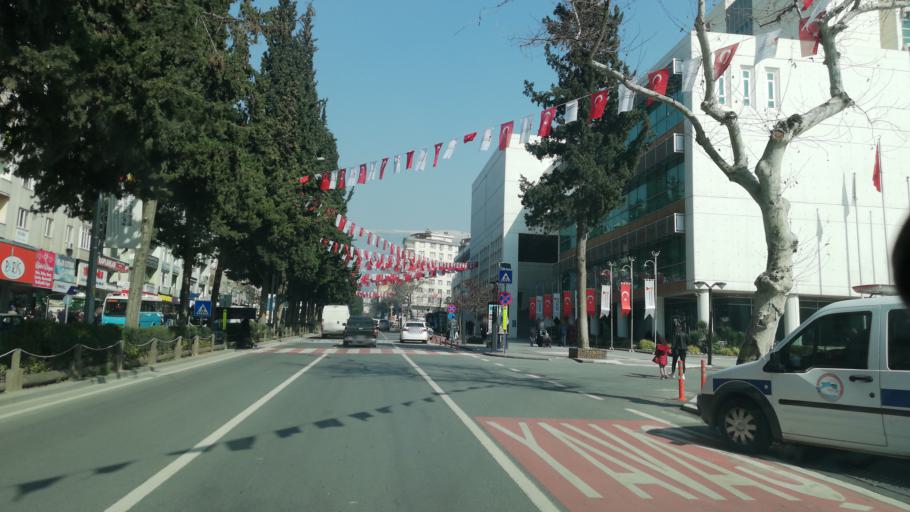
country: TR
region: Kahramanmaras
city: Kahramanmaras
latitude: 37.5757
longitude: 36.9264
